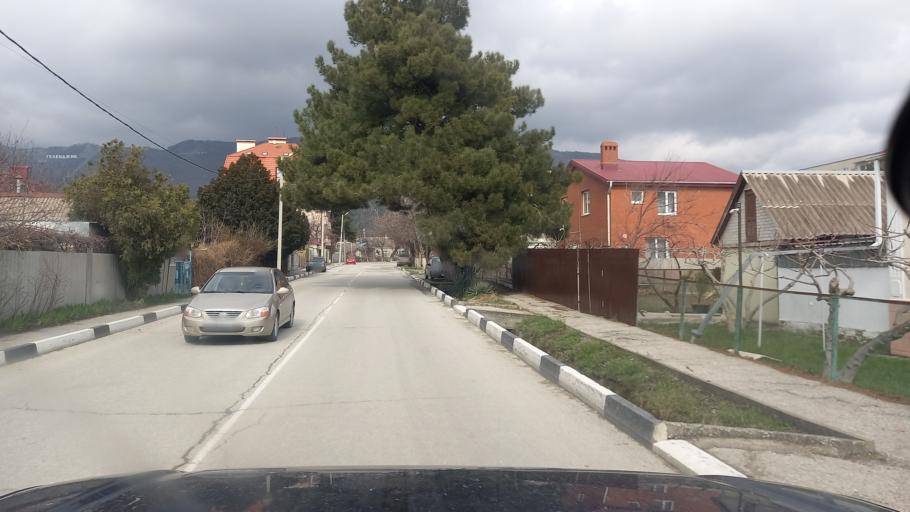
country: RU
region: Krasnodarskiy
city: Gelendzhik
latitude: 44.5584
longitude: 38.0900
